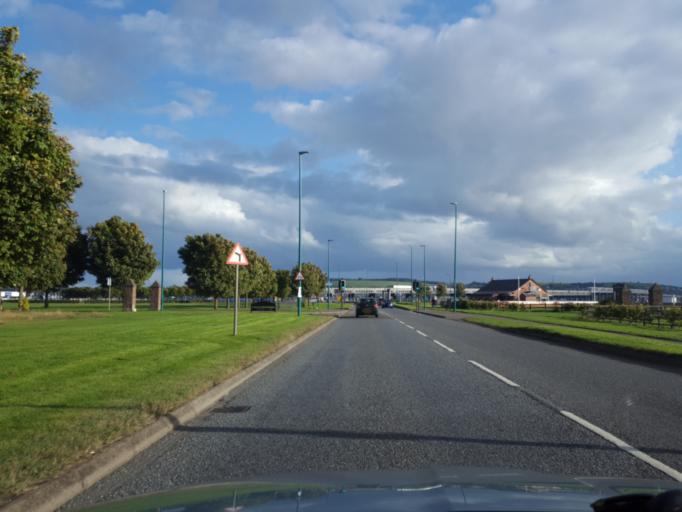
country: GB
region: Scotland
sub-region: Dundee City
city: Dundee
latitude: 56.4531
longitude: -2.9998
